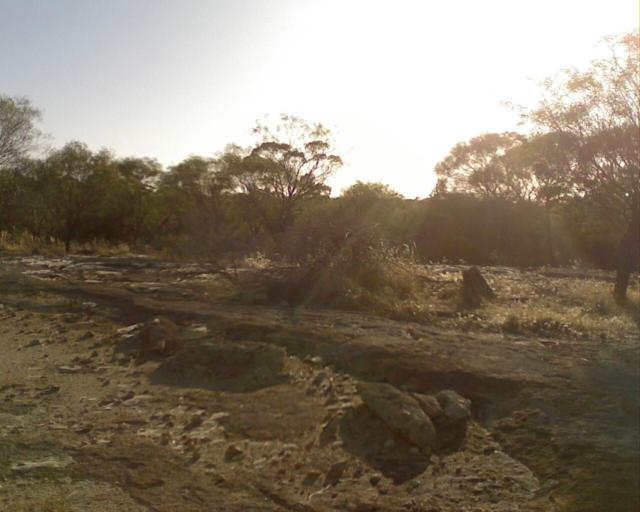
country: AU
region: Western Australia
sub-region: Merredin
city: Merredin
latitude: -30.9494
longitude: 117.8607
